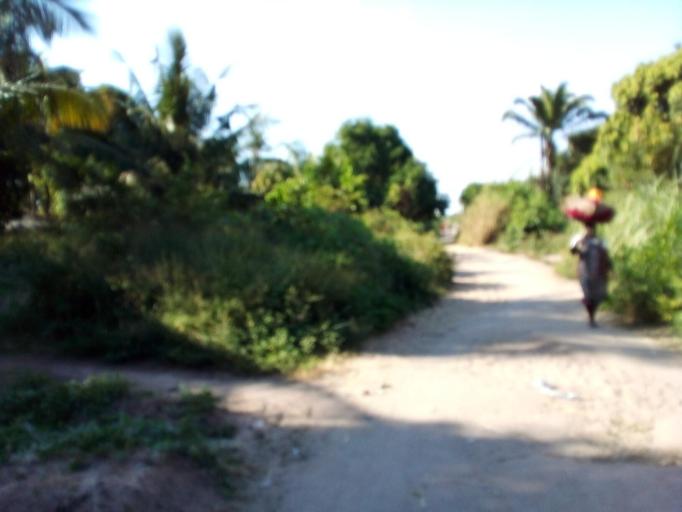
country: MZ
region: Zambezia
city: Quelimane
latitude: -17.5970
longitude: 36.8286
